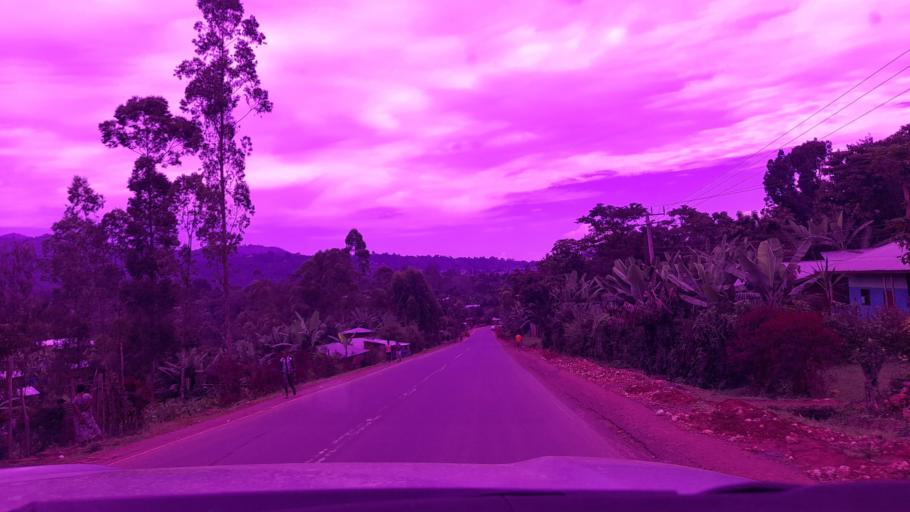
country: ET
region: Southern Nations, Nationalities, and People's Region
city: Mizan Teferi
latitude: 7.0046
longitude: 35.6053
